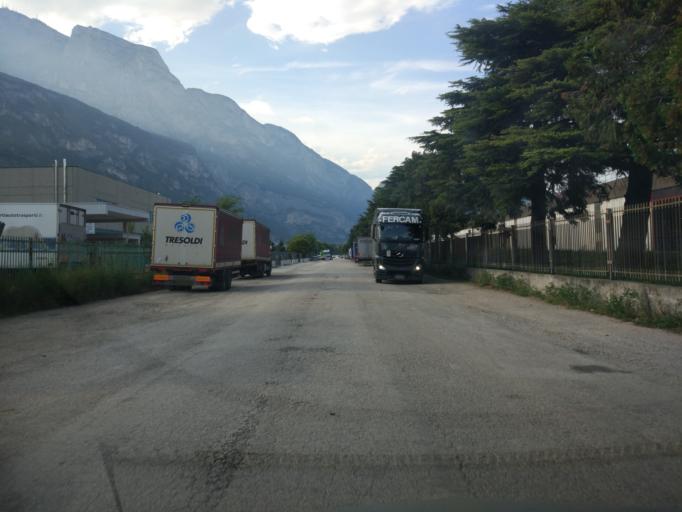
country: IT
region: Trentino-Alto Adige
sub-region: Provincia di Trento
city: Meano
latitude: 46.1152
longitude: 11.0954
